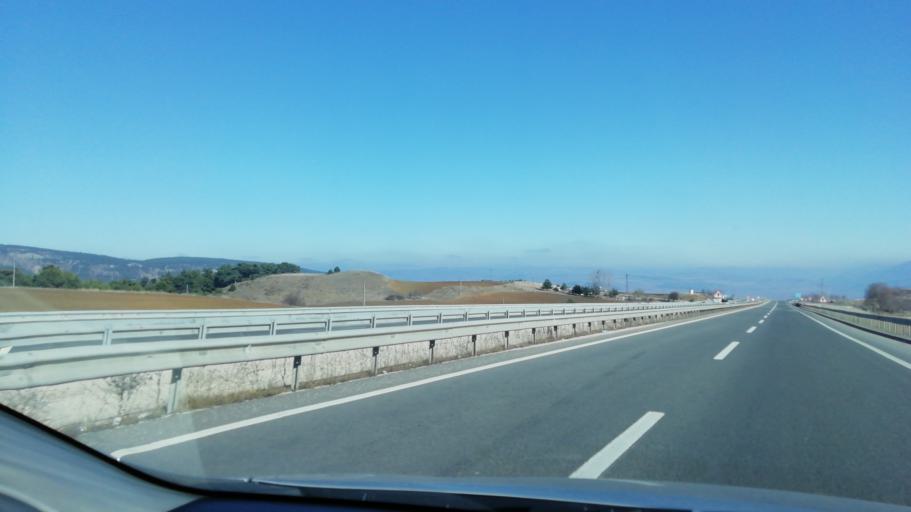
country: TR
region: Karabuk
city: Gozyeri
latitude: 40.8591
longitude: 32.5371
